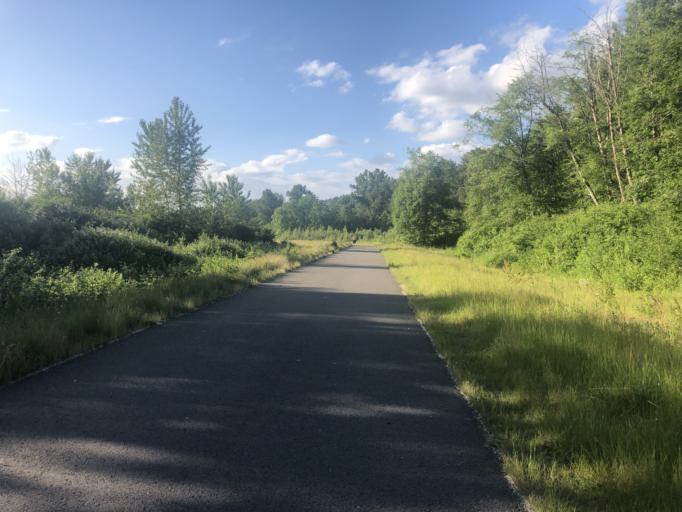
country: US
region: Washington
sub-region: King County
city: Lea Hill
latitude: 47.3418
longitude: -122.2076
